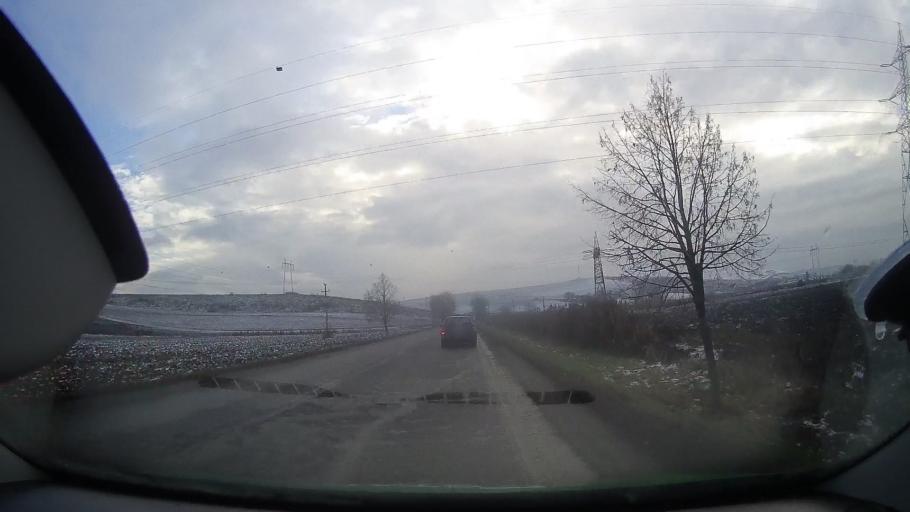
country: RO
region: Mures
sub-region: Comuna Cucerdea
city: Cucerdea
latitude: 46.4231
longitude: 24.2595
